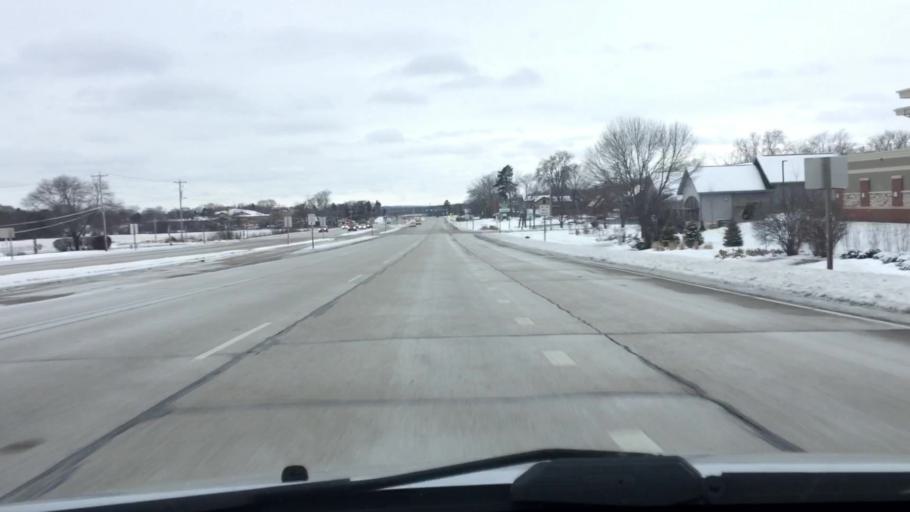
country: US
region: Wisconsin
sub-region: Waukesha County
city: Brookfield
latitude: 43.0903
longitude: -88.1289
